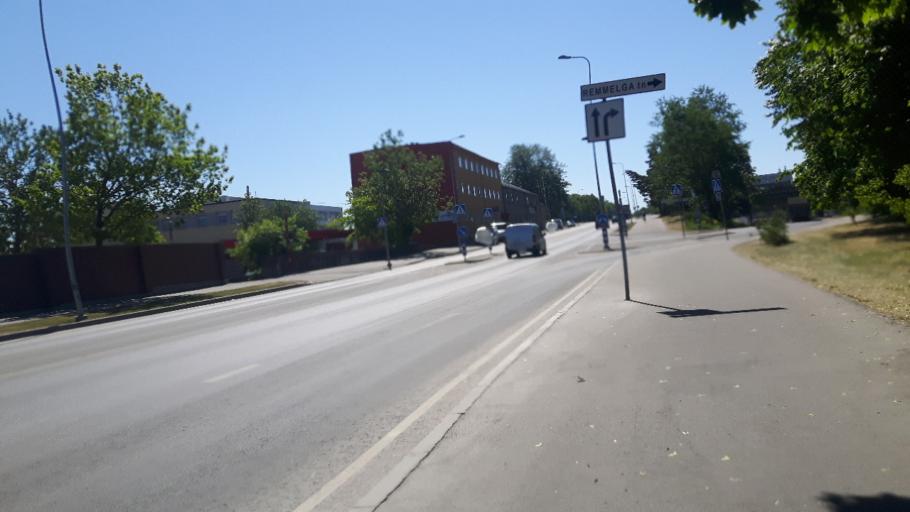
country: EE
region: Harju
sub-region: Tallinna linn
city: Tallinn
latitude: 59.3712
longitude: 24.7171
